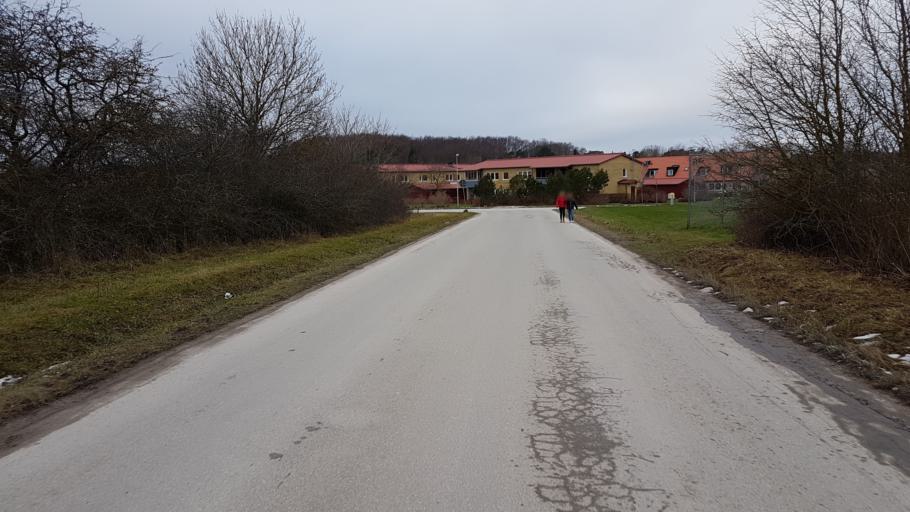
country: SE
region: Gotland
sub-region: Gotland
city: Visby
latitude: 57.6214
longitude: 18.3142
